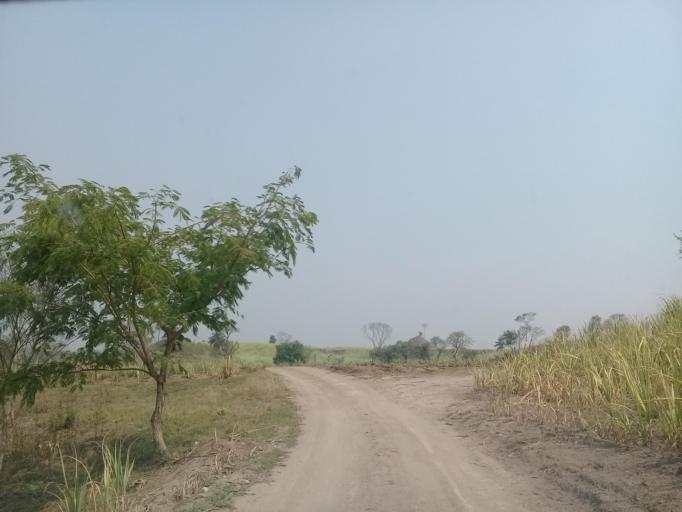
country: MX
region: Oaxaca
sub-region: Acatlan de Perez Figueroa
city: Zona Urbana Ejidal
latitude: 18.5905
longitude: -96.5618
